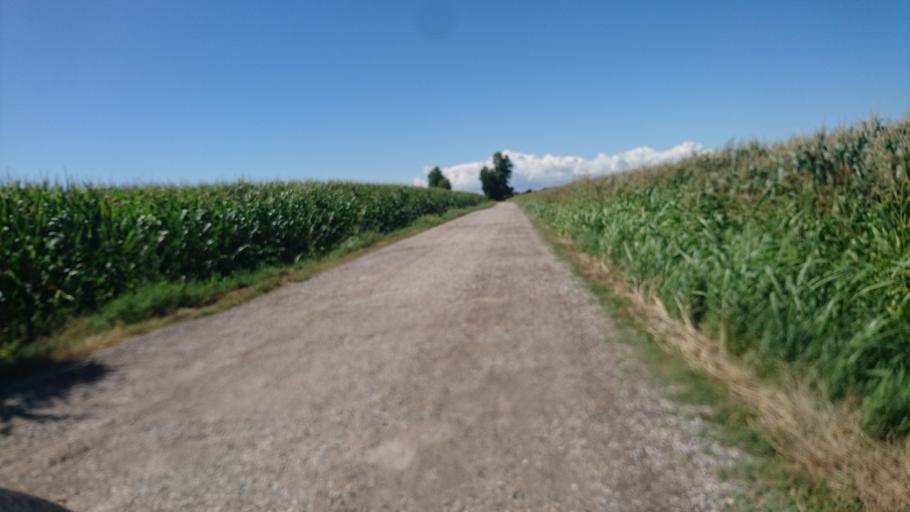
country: IT
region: Veneto
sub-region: Provincia di Padova
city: Pontelongo
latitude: 45.2612
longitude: 12.0156
